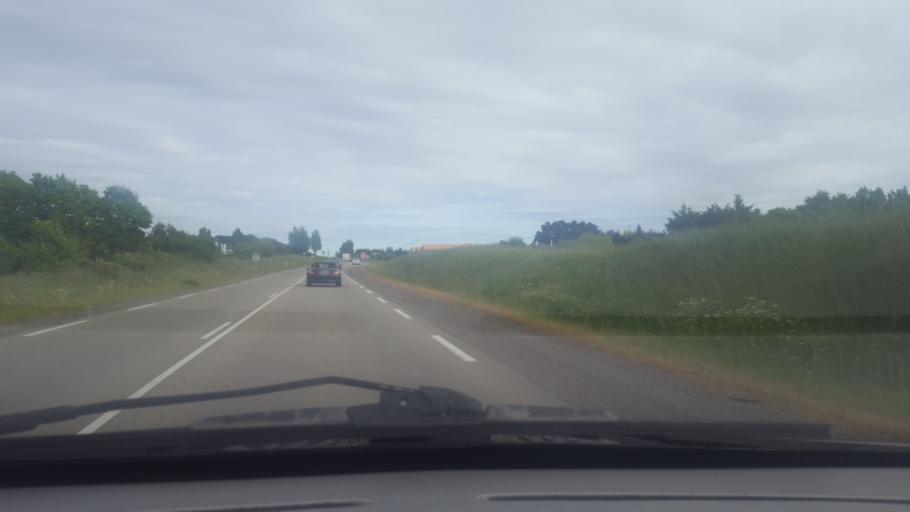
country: FR
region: Pays de la Loire
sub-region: Departement de la Loire-Atlantique
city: Bourgneuf-en-Retz
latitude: 47.0528
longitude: -1.9662
